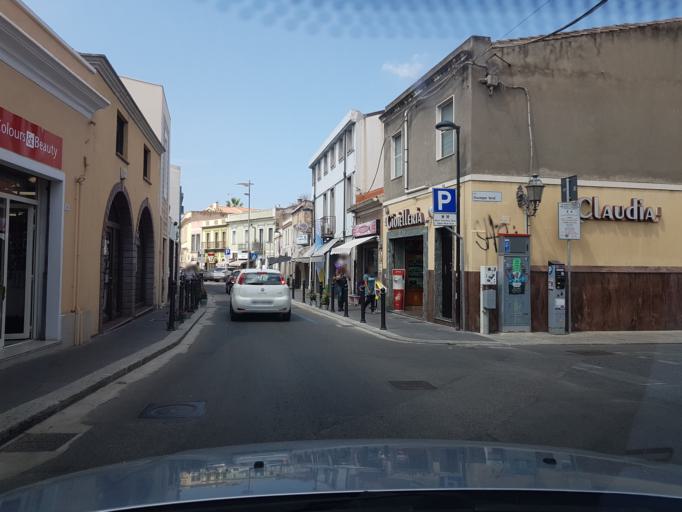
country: IT
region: Sardinia
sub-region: Provincia di Oristano
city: Oristano
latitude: 39.9067
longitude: 8.5930
